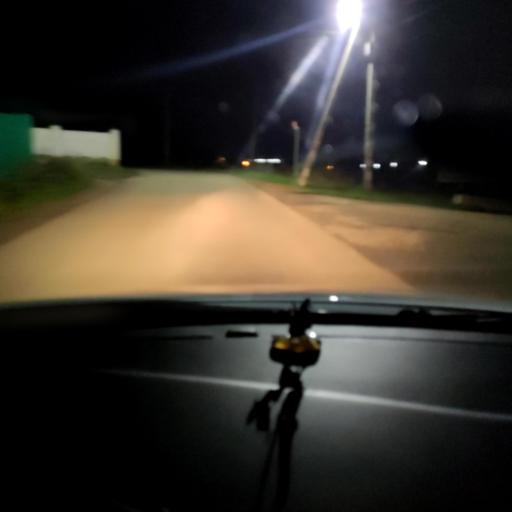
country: RU
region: Tatarstan
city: Vysokaya Gora
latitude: 55.8951
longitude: 49.3044
